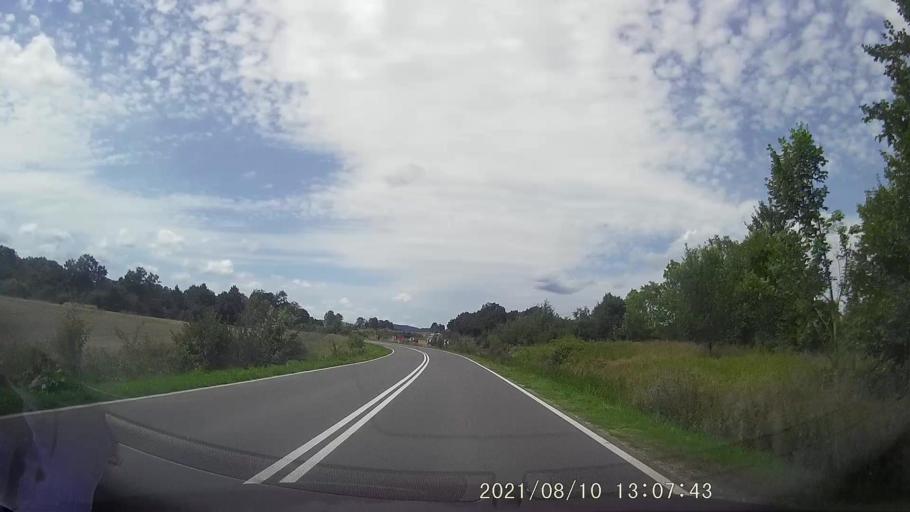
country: PL
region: Lower Silesian Voivodeship
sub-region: Powiat klodzki
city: Bozkow
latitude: 50.4896
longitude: 16.5701
